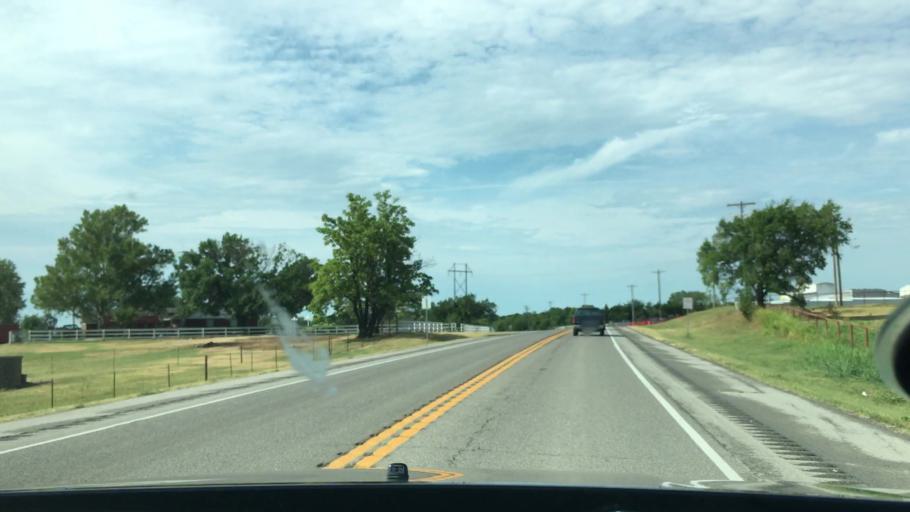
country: US
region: Oklahoma
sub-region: Murray County
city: Sulphur
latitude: 34.5297
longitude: -96.9683
